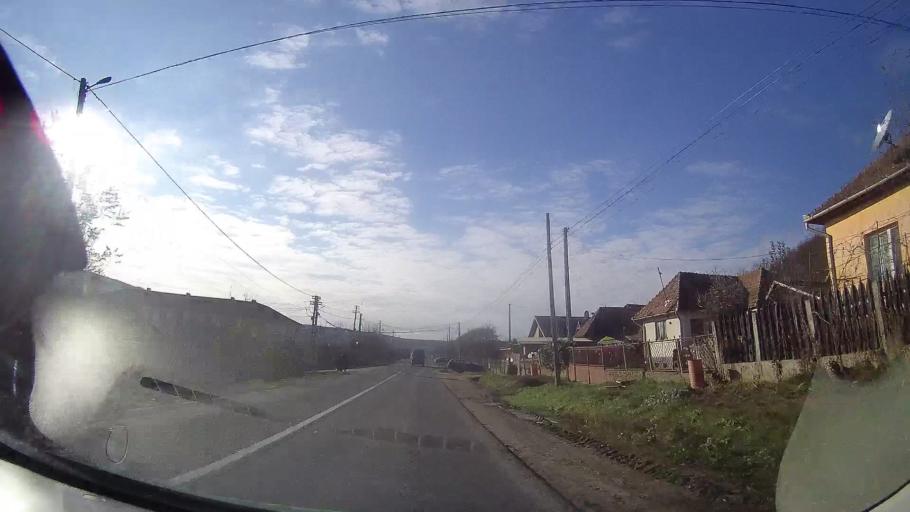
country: RO
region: Cluj
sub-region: Comuna Caianu
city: Caianu
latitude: 46.7972
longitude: 23.9175
